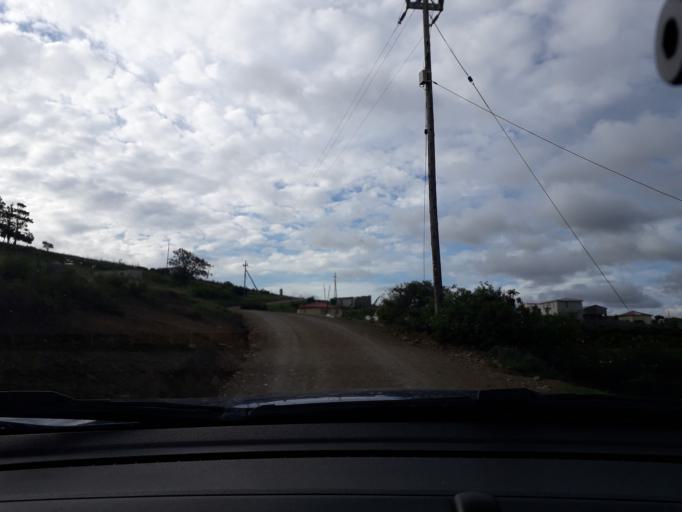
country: ZA
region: Eastern Cape
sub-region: Buffalo City Metropolitan Municipality
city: East London
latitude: -32.8011
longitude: 27.9623
